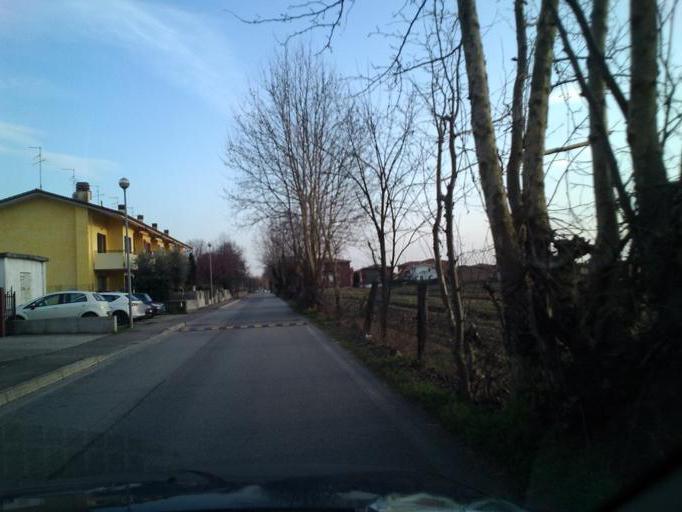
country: IT
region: Veneto
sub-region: Provincia di Verona
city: Caselle
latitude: 45.4185
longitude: 10.8937
